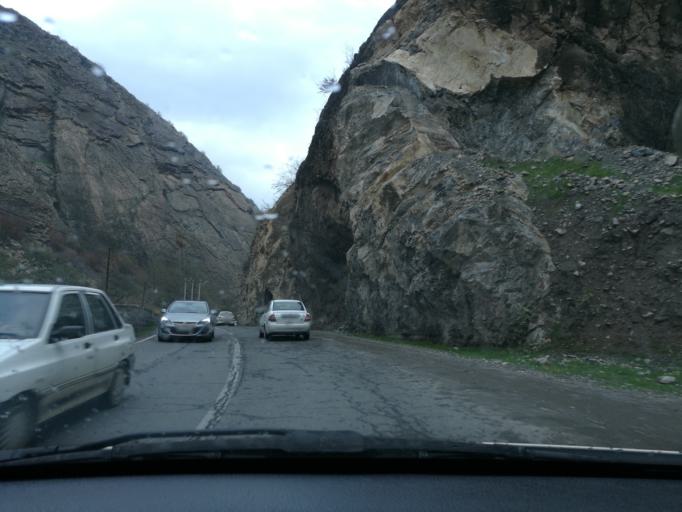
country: IR
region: Mazandaran
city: Chalus
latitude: 36.3183
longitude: 51.2500
